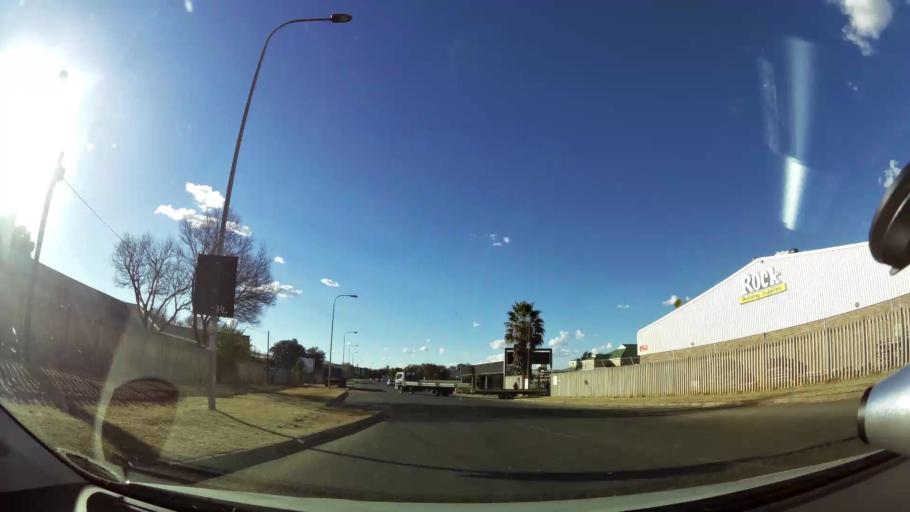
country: ZA
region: North-West
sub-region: Dr Kenneth Kaunda District Municipality
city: Klerksdorp
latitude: -26.8630
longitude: 26.6690
